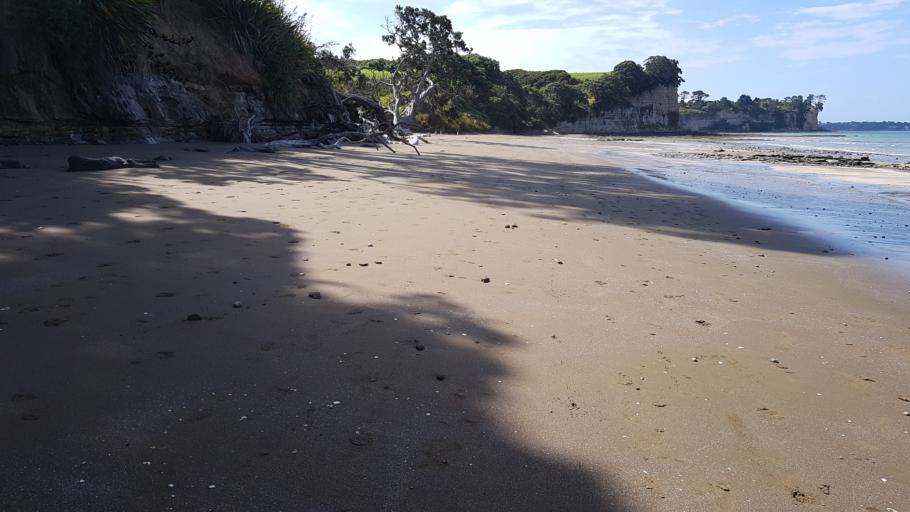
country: NZ
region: Auckland
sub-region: Auckland
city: Rothesay Bay
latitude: -36.6756
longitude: 174.7479
